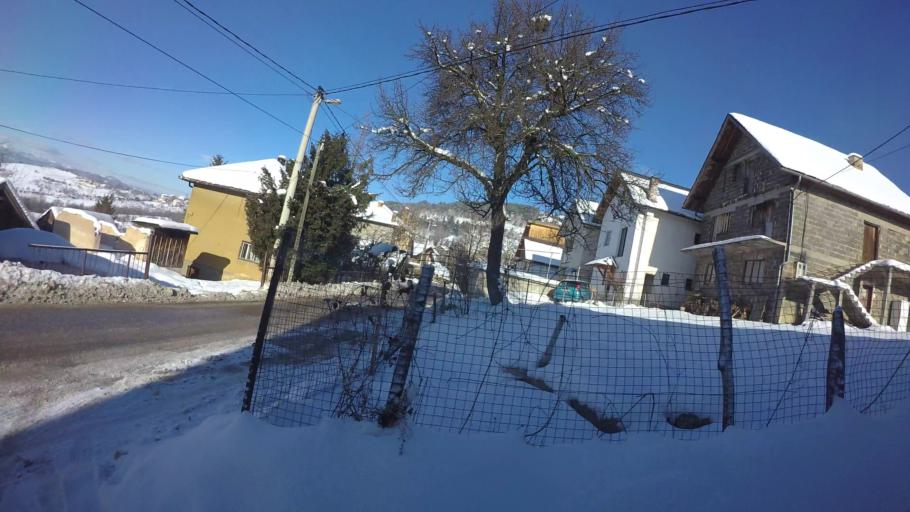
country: BA
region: Federation of Bosnia and Herzegovina
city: Kobilja Glava
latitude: 43.8910
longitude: 18.4087
